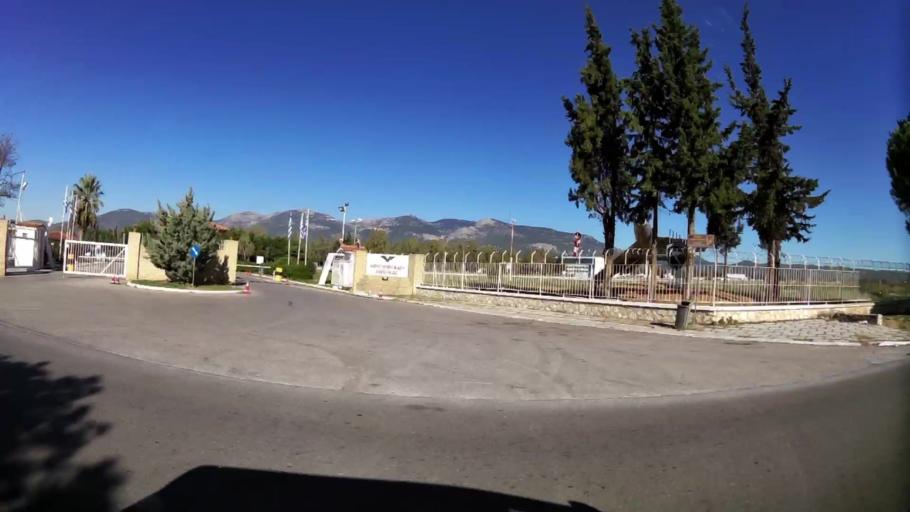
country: GR
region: Attica
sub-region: Nomarchia Anatolikis Attikis
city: Varybobi
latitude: 38.1006
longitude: 23.7797
